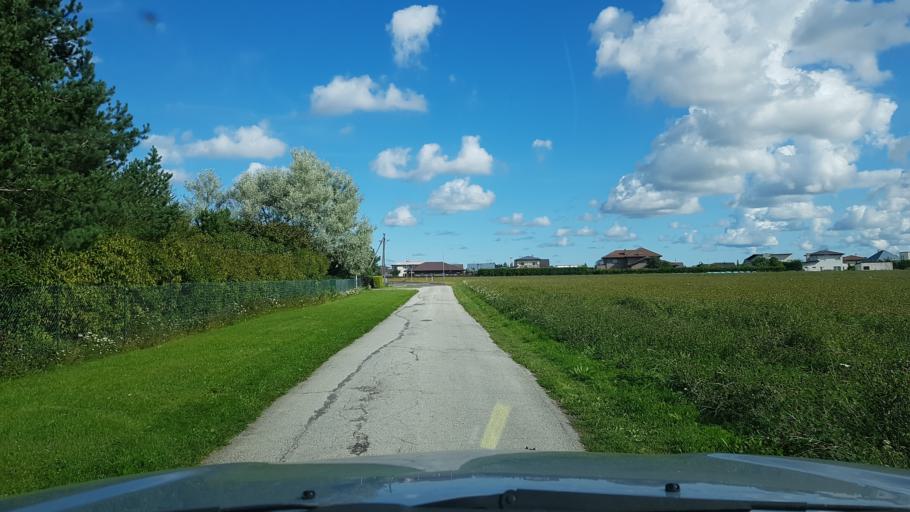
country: EE
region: Harju
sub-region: Tallinna linn
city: Tallinn
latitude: 59.3866
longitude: 24.7996
